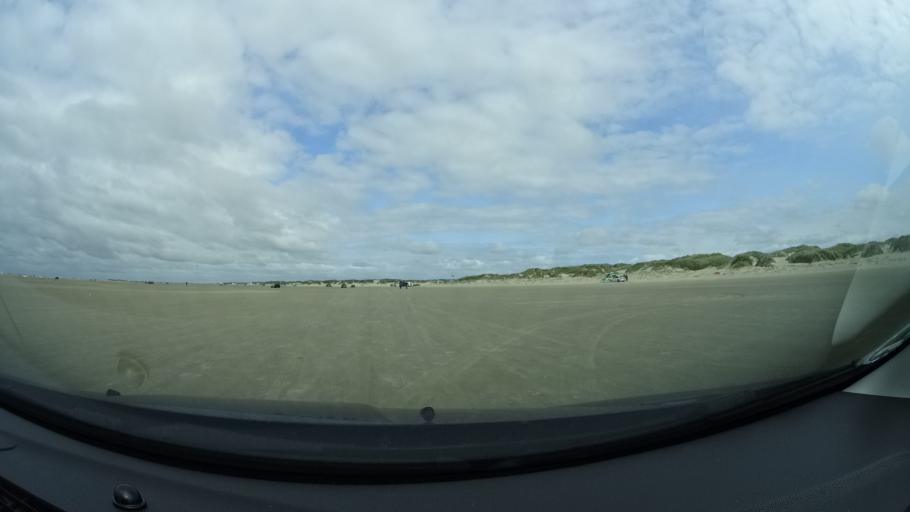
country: DE
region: Schleswig-Holstein
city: List
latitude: 55.1425
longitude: 8.4852
